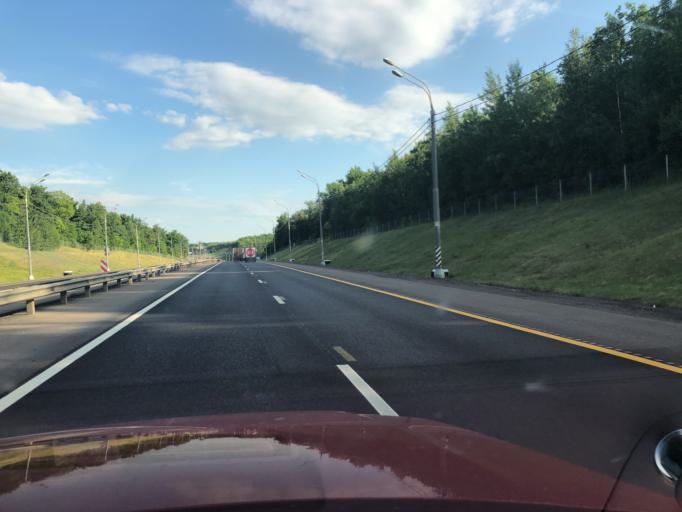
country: RU
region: Lipetsk
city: Zadonsk
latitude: 52.3979
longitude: 38.8604
